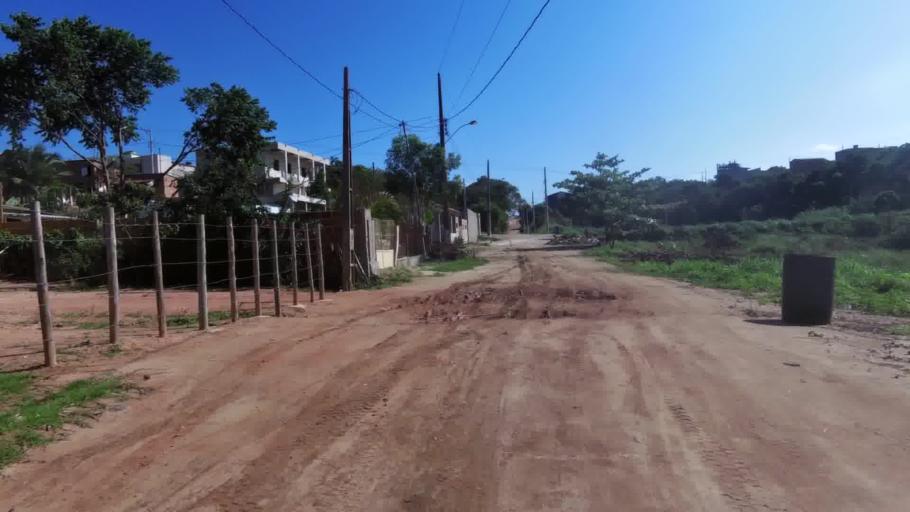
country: BR
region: Espirito Santo
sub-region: Piuma
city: Piuma
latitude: -20.8192
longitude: -40.6207
